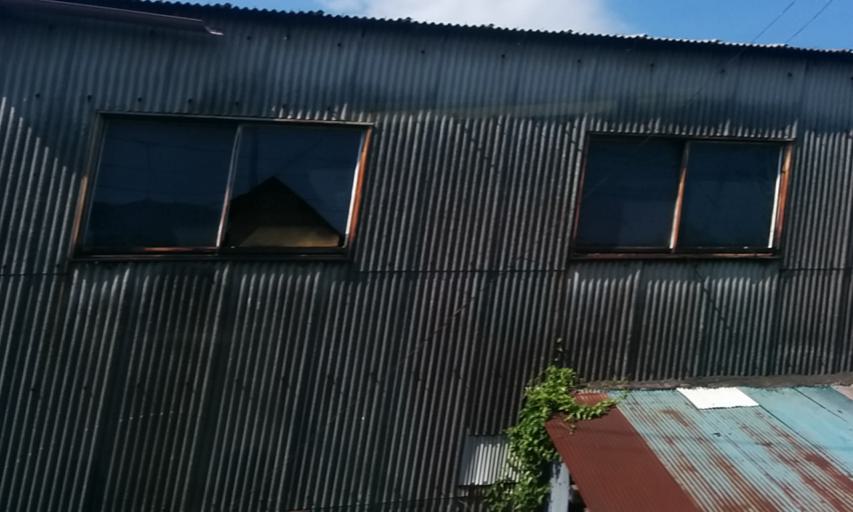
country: JP
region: Saitama
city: Kazo
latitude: 36.1308
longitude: 139.5841
